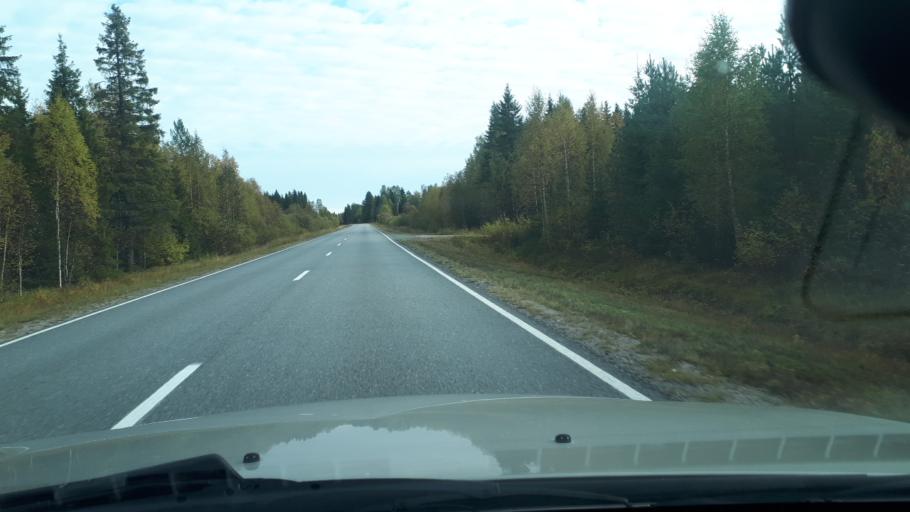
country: FI
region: Lapland
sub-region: Rovaniemi
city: Rovaniemi
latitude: 65.9531
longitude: 25.9215
